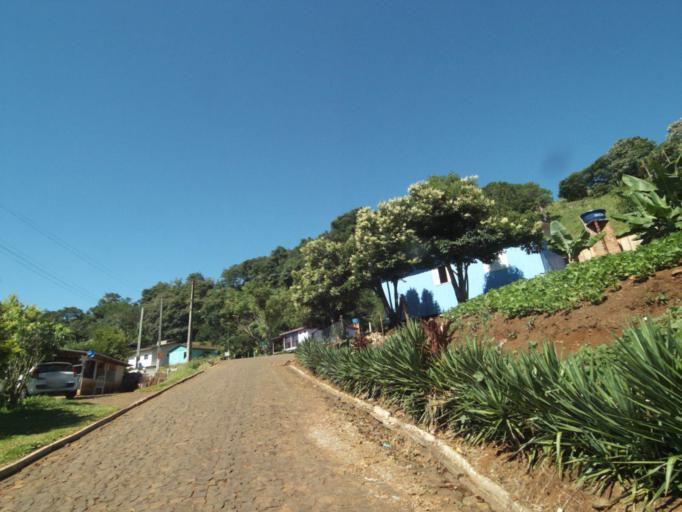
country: BR
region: Parana
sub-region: Ampere
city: Ampere
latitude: -26.1691
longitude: -53.3601
